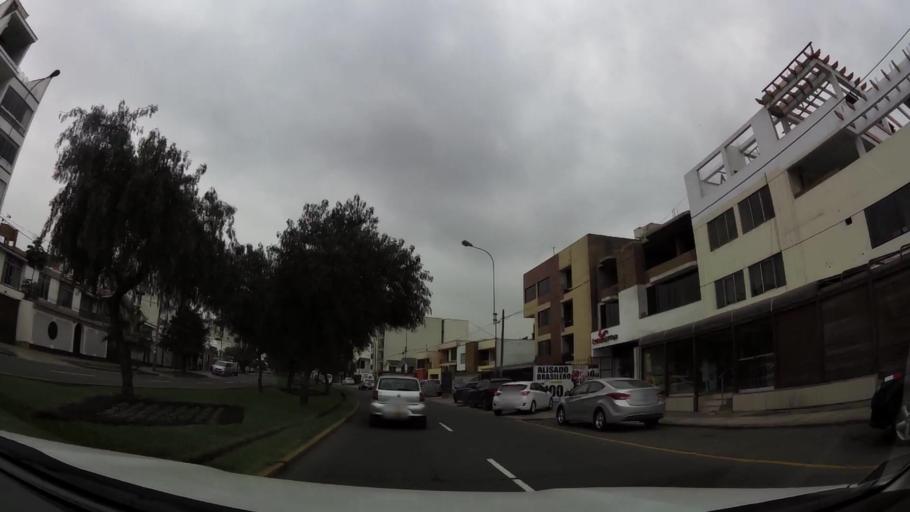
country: PE
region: Lima
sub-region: Lima
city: San Luis
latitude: -12.1063
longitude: -76.9921
